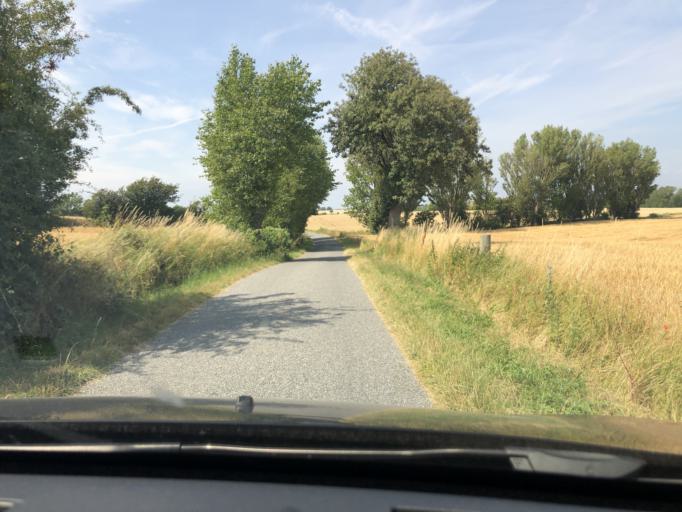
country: DK
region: South Denmark
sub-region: AEro Kommune
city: AEroskobing
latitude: 54.9070
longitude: 10.2975
